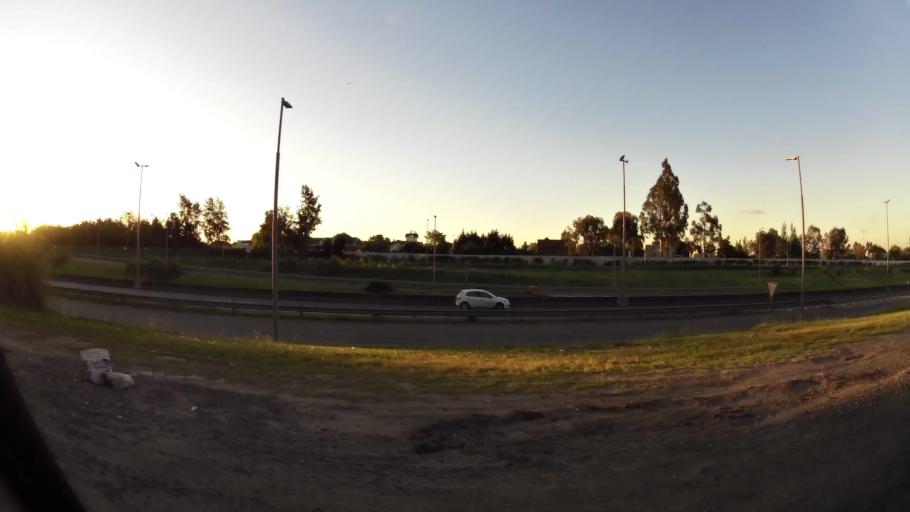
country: AR
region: Buenos Aires
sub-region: Partido de Quilmes
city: Quilmes
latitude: -34.8005
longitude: -58.1633
